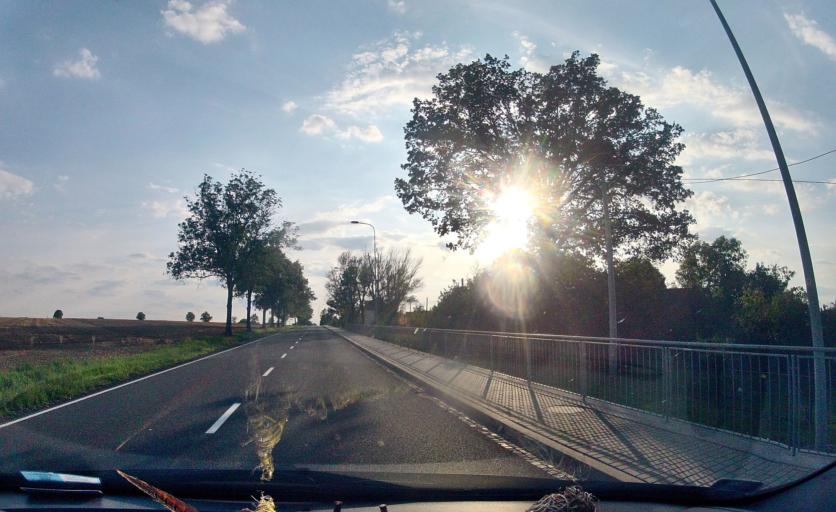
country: PL
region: Opole Voivodeship
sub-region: Powiat oleski
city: Gorzow Slaski
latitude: 51.0122
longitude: 18.3753
